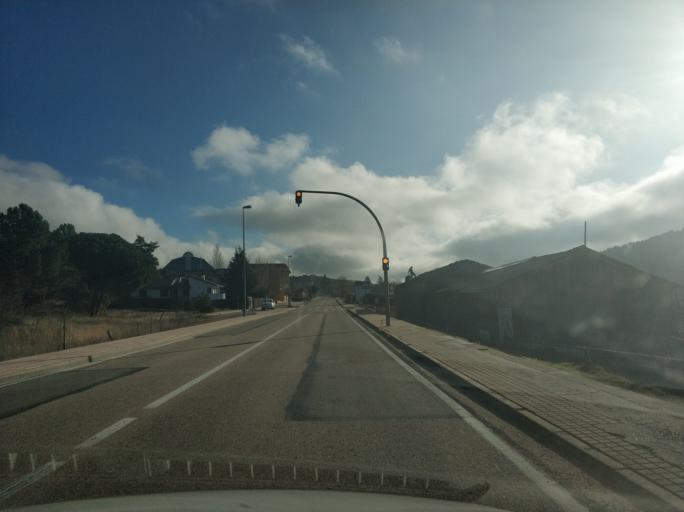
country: ES
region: Castille and Leon
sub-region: Provincia de Soria
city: Navaleno
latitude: 41.8374
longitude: -3.0118
